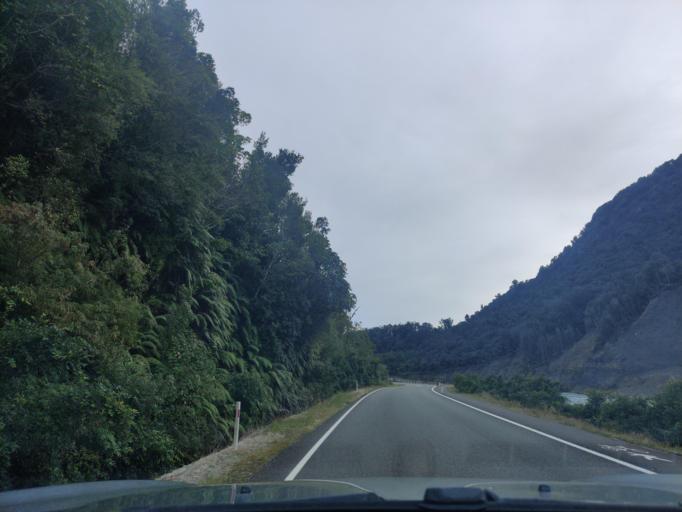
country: NZ
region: West Coast
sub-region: Westland District
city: Hokitika
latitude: -43.3989
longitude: 170.1808
